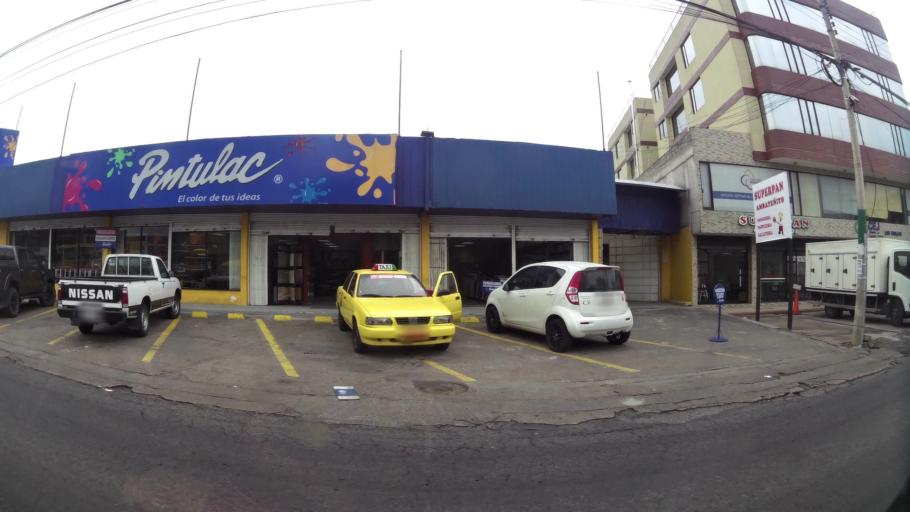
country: EC
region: Pichincha
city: Sangolqui
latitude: -0.2972
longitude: -78.4614
